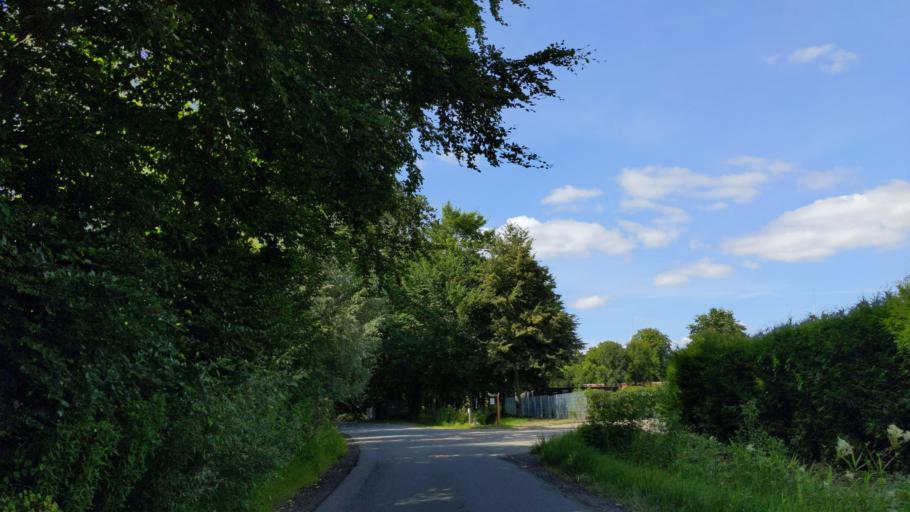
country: DE
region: Schleswig-Holstein
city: Altenkrempe
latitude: 54.1557
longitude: 10.8318
